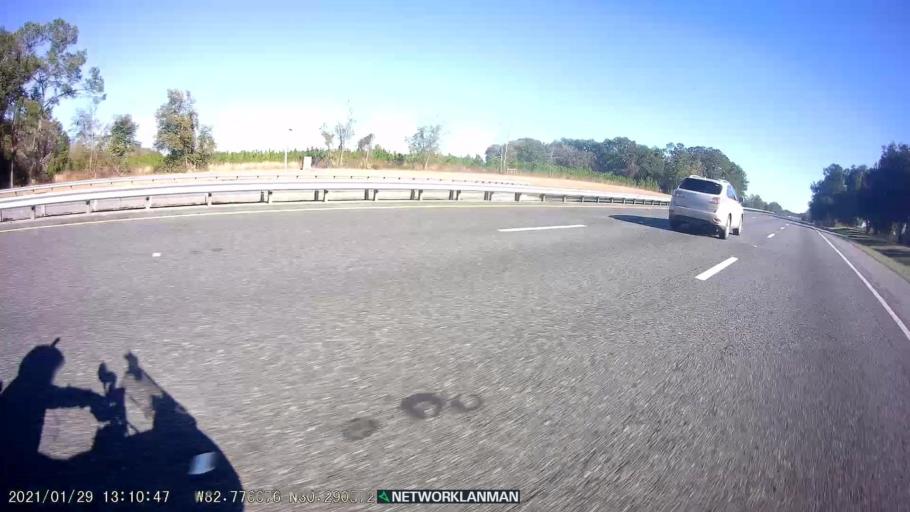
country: US
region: Florida
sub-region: Suwannee County
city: Wellborn
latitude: 30.2905
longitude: -82.7757
